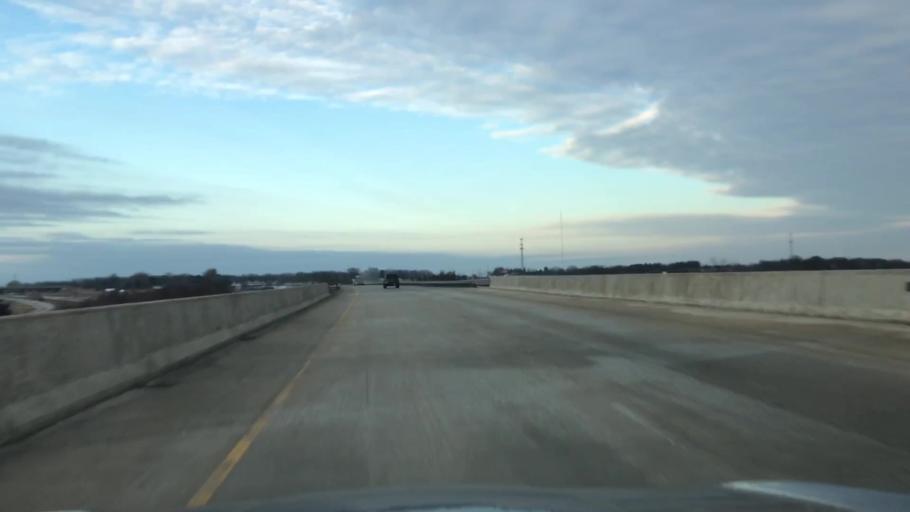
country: US
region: Illinois
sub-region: McLean County
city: Bloomington
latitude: 40.4390
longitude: -89.0238
